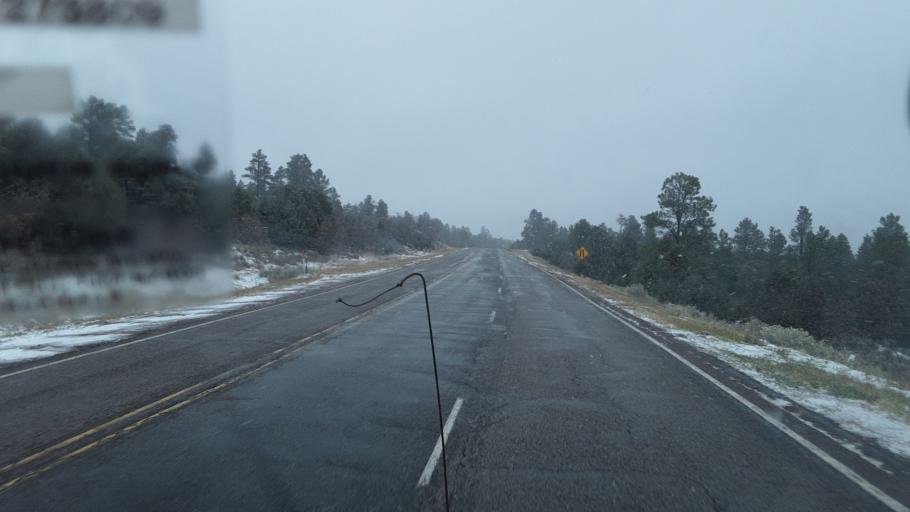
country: US
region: New Mexico
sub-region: Rio Arriba County
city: Tierra Amarilla
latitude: 36.6665
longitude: -106.5570
